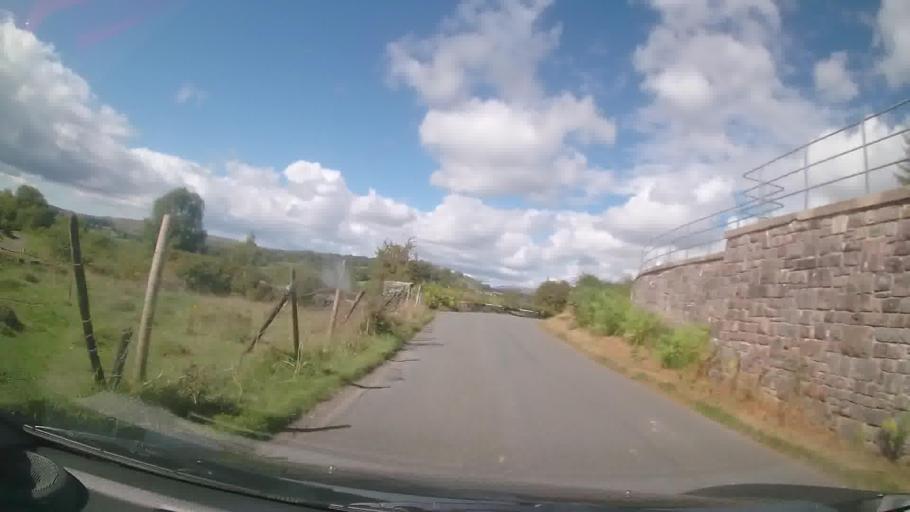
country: GB
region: Wales
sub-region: Merthyr Tydfil County Borough
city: Merthyr Tydfil
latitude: 51.7791
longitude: -3.3656
